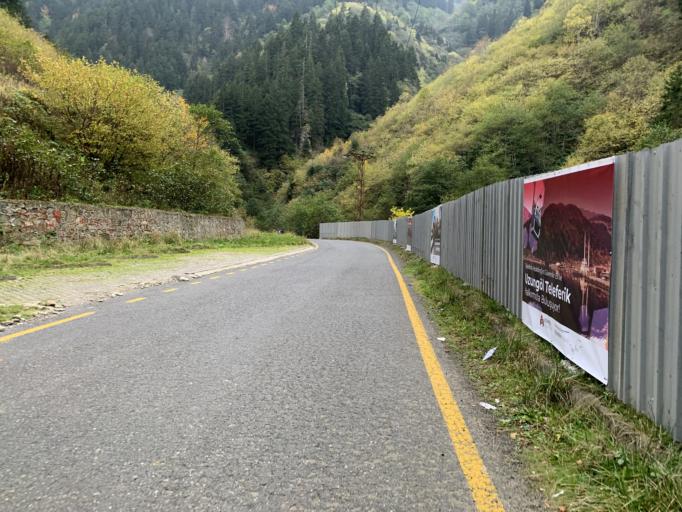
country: TR
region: Trabzon
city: Uzungol
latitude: 40.5942
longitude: 40.3209
